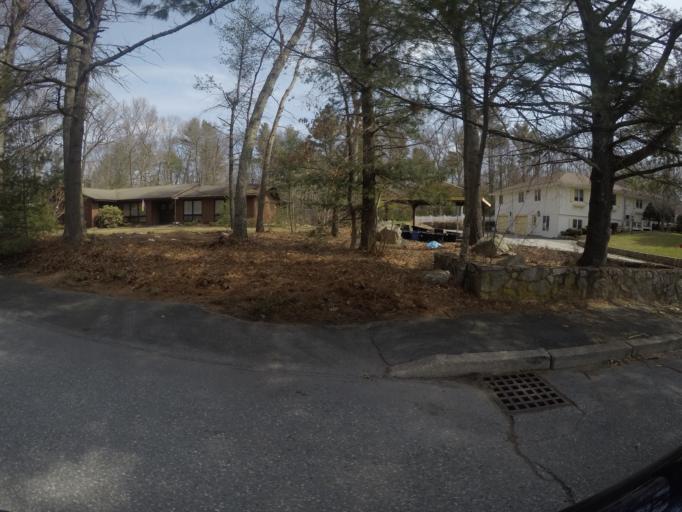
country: US
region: Massachusetts
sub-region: Bristol County
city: Easton
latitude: 42.0507
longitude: -71.1251
